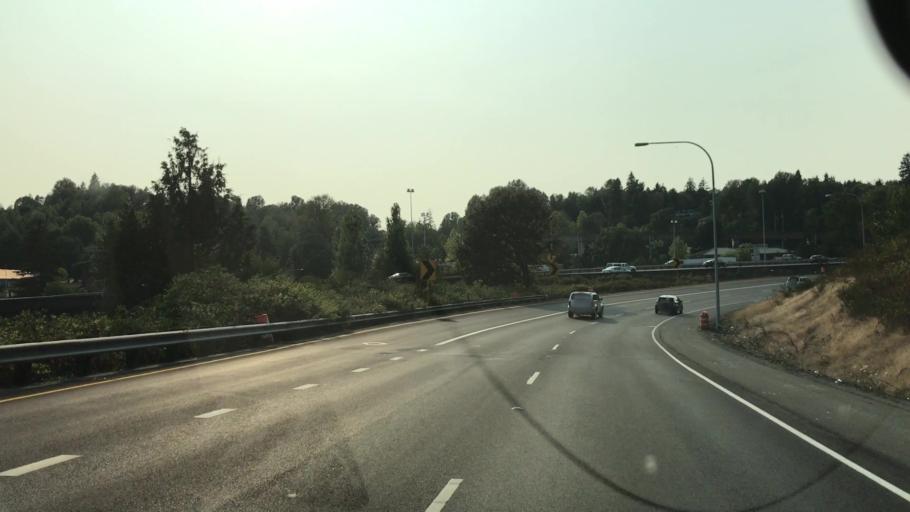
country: US
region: Washington
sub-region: King County
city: Tukwila
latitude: 47.4652
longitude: -122.2645
